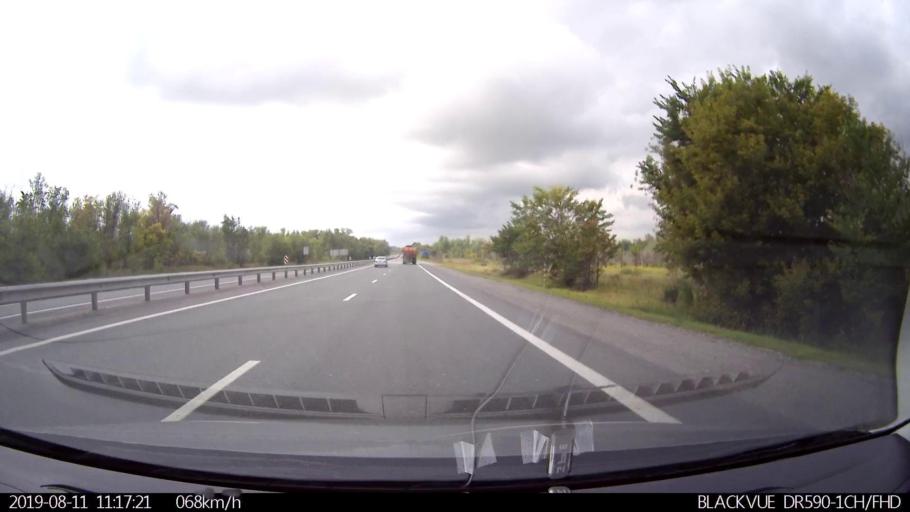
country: RU
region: Ulyanovsk
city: Novoul'yanovsk
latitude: 54.1896
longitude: 48.2777
